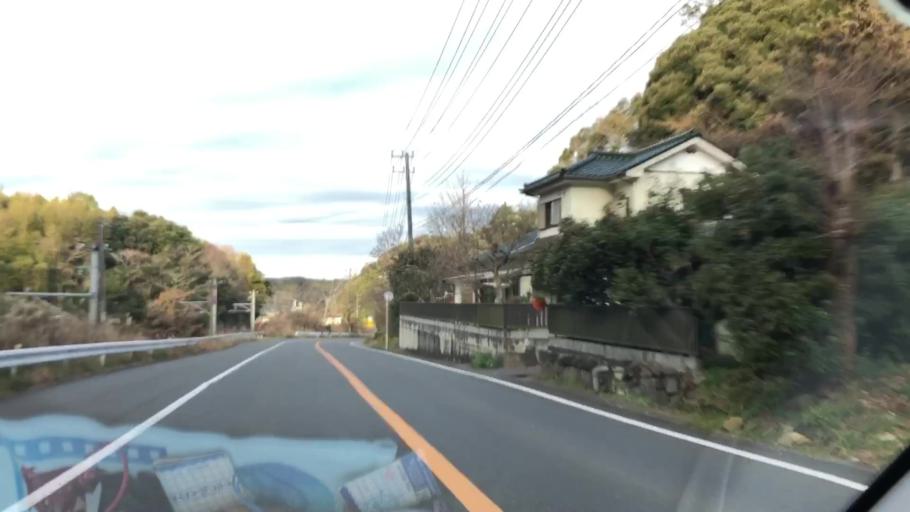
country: JP
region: Chiba
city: Tateyama
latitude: 34.9888
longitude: 139.9289
